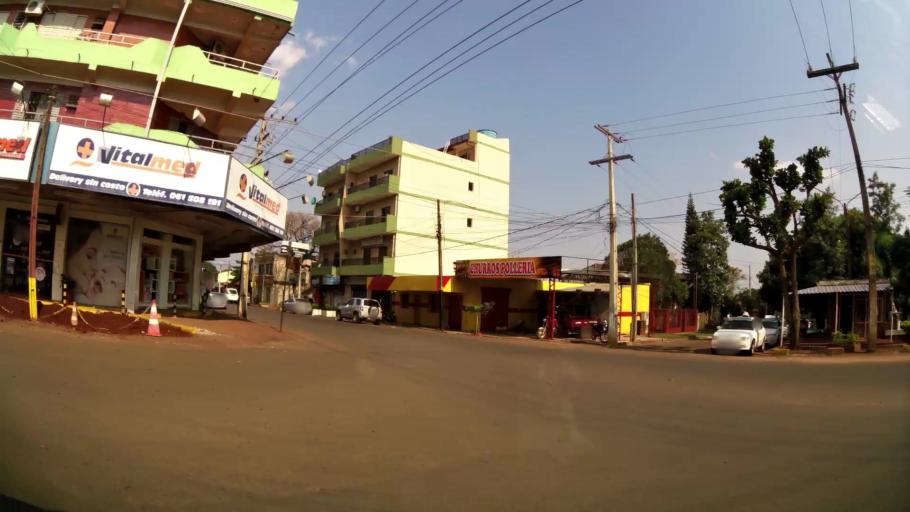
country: PY
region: Alto Parana
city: Presidente Franco
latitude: -25.5360
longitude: -54.6240
